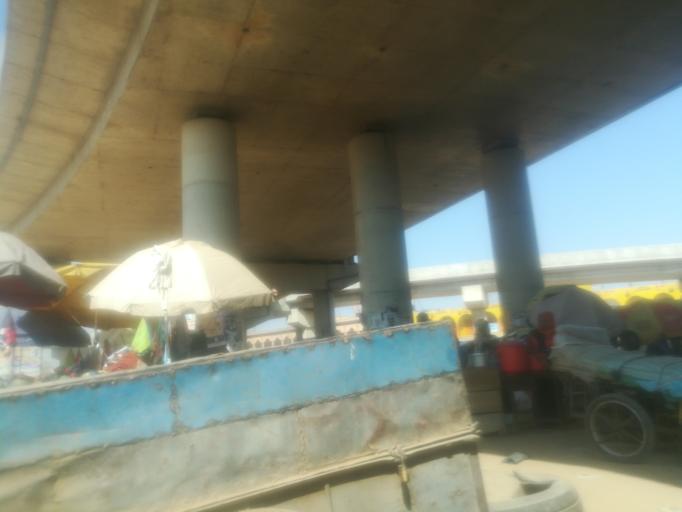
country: NG
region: Kano
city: Kano
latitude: 12.0099
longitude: 8.5395
